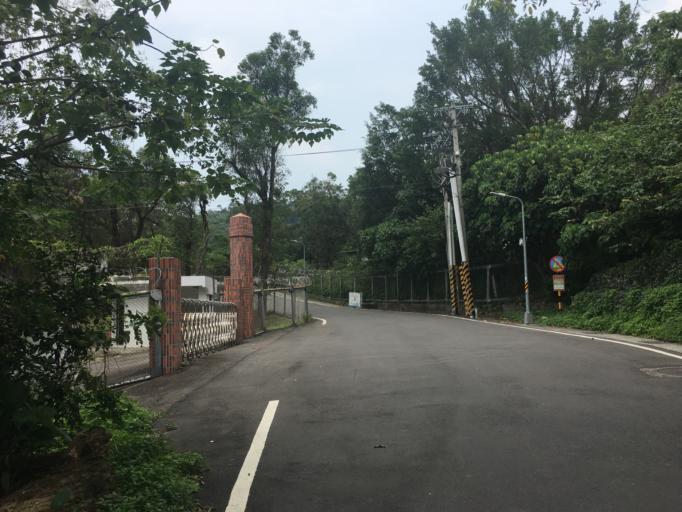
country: TW
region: Taipei
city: Taipei
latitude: 25.0884
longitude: 121.5540
